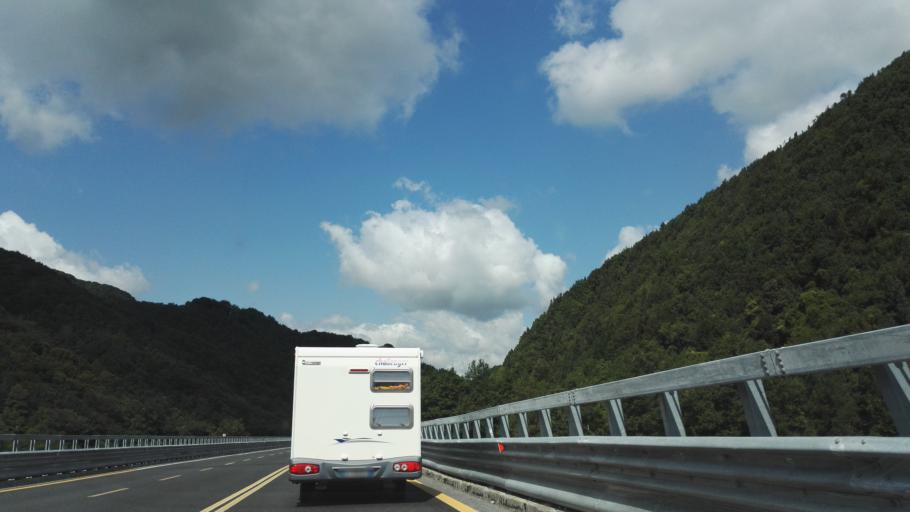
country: IT
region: Calabria
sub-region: Provincia di Reggio Calabria
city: Amato
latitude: 38.4051
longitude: 16.1535
